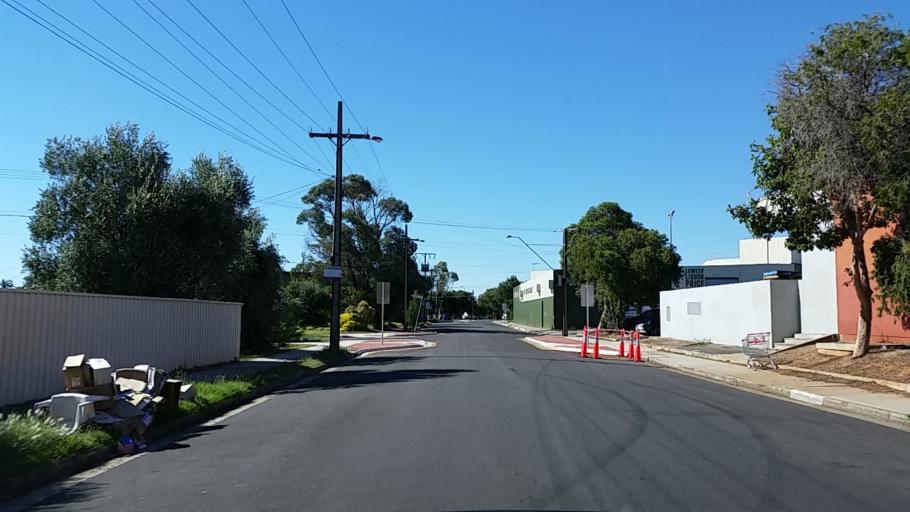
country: AU
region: South Australia
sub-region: Charles Sturt
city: Allenby Gardens
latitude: -34.8966
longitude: 138.5563
